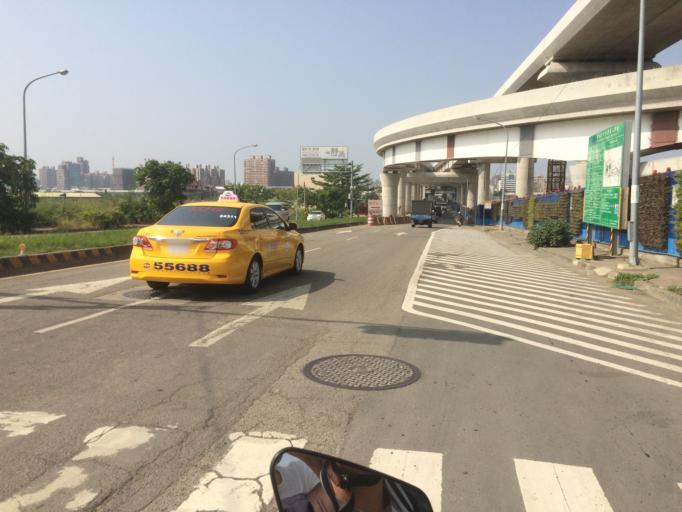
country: TW
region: Taiwan
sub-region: Taichung City
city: Taichung
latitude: 24.1824
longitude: 120.7106
